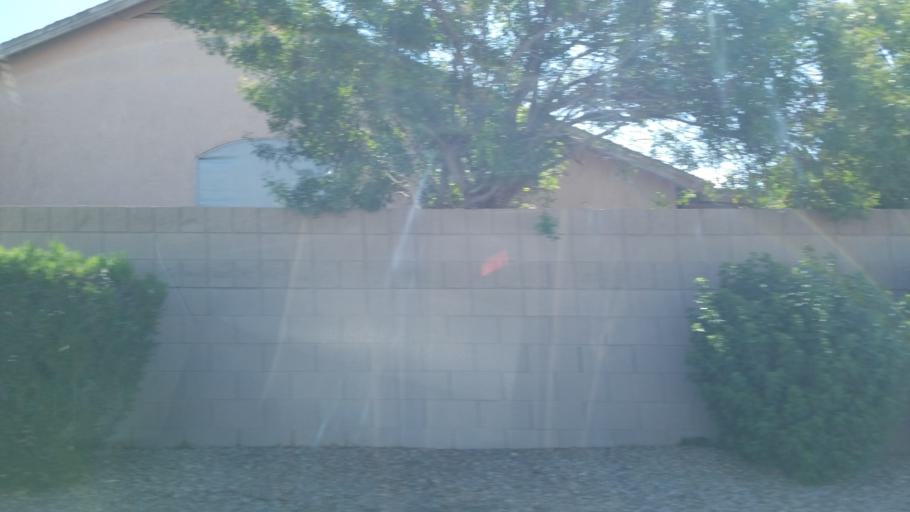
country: US
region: Arizona
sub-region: Maricopa County
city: Peoria
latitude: 33.6813
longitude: -112.1434
